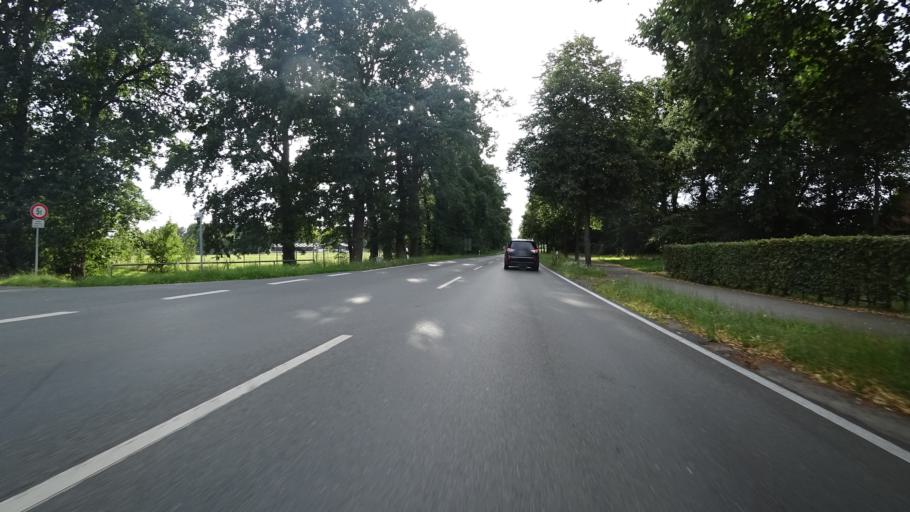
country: DE
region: North Rhine-Westphalia
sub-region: Regierungsbezirk Detmold
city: Harsewinkel
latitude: 51.9644
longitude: 8.2016
